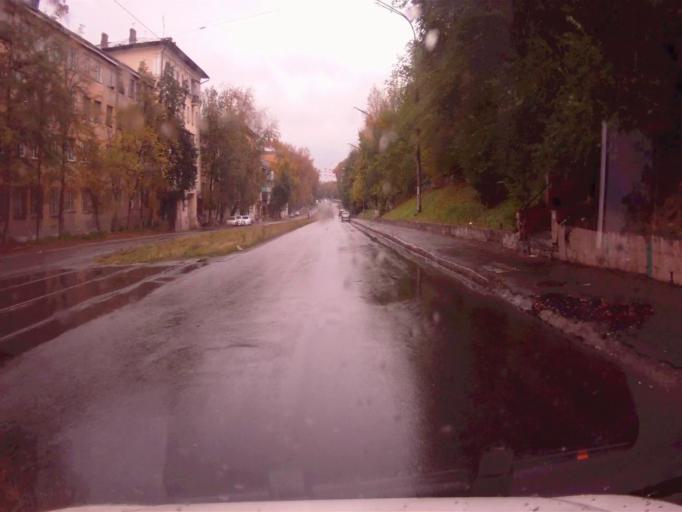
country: RU
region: Chelyabinsk
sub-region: Gorod Chelyabinsk
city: Chelyabinsk
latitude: 55.1863
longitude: 61.4139
